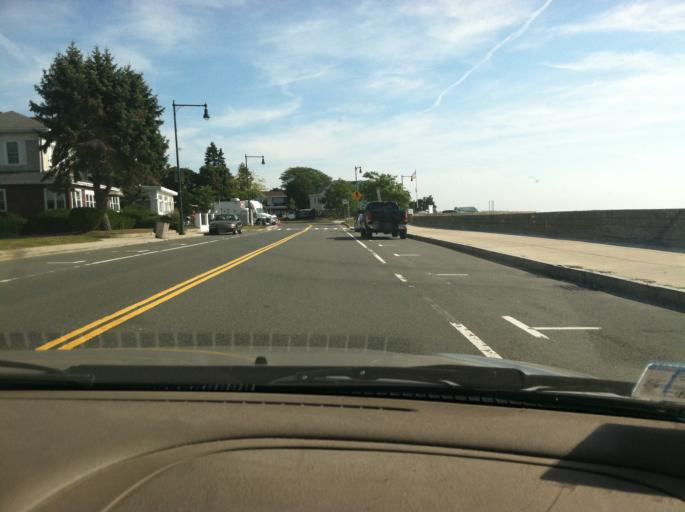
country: US
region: Massachusetts
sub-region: Suffolk County
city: Revere
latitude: 42.4312
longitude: -70.9764
